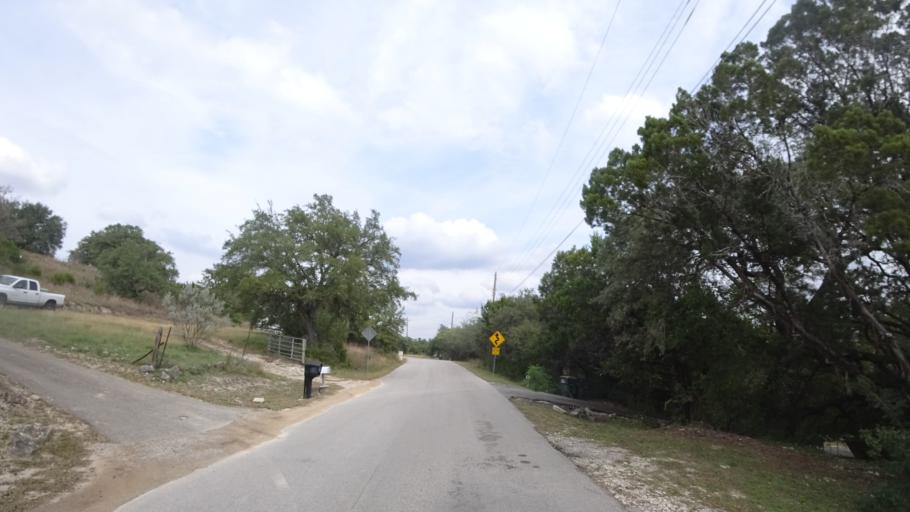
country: US
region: Texas
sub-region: Travis County
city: Hudson Bend
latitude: 30.3729
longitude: -97.9177
